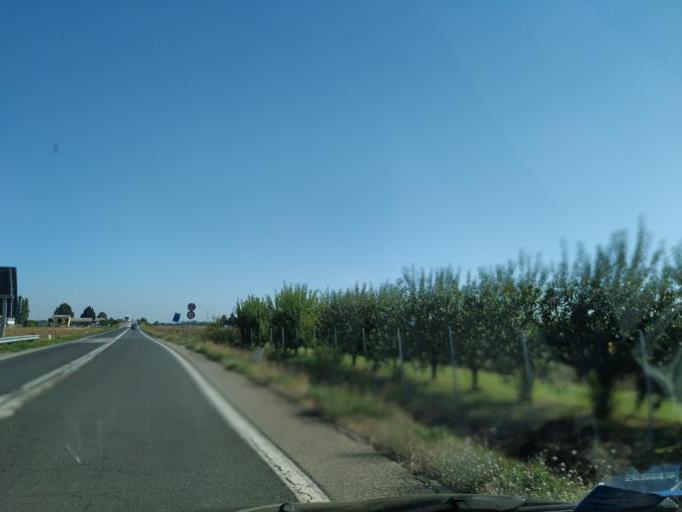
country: IT
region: Emilia-Romagna
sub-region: Provincia di Bologna
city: Decima
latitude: 44.6997
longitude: 11.2359
